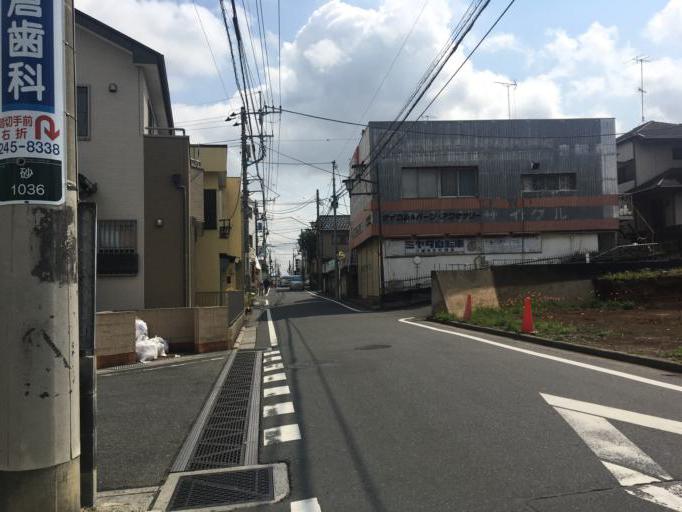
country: JP
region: Saitama
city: Kamifukuoka
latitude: 35.8906
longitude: 139.5011
